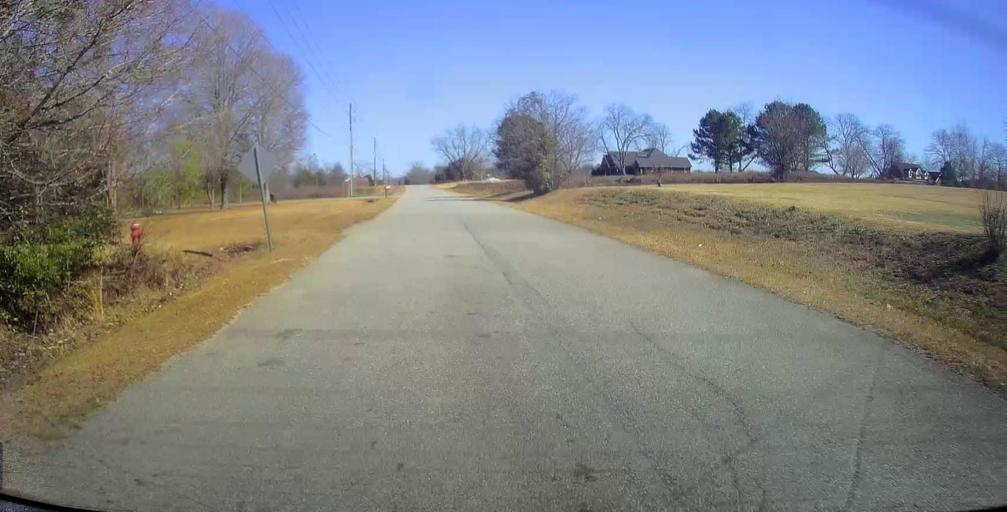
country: US
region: Georgia
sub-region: Peach County
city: Byron
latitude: 32.6357
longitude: -83.7661
